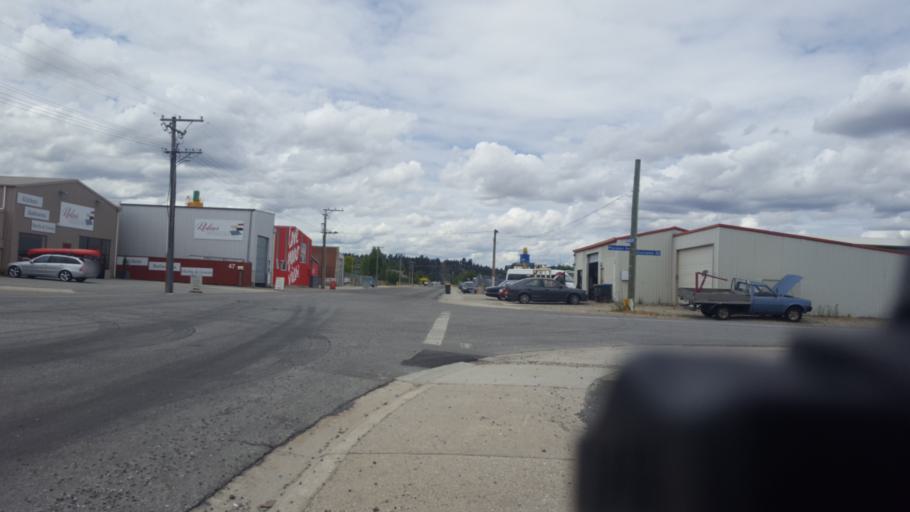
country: NZ
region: Otago
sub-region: Queenstown-Lakes District
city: Wanaka
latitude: -45.2480
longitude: 169.3728
